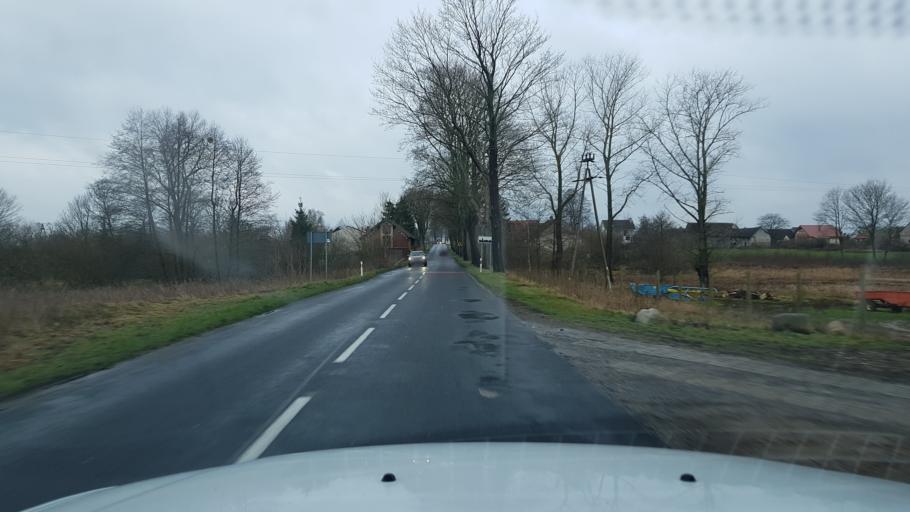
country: PL
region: West Pomeranian Voivodeship
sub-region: Powiat gryficki
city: Brojce
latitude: 54.0625
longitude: 15.3922
